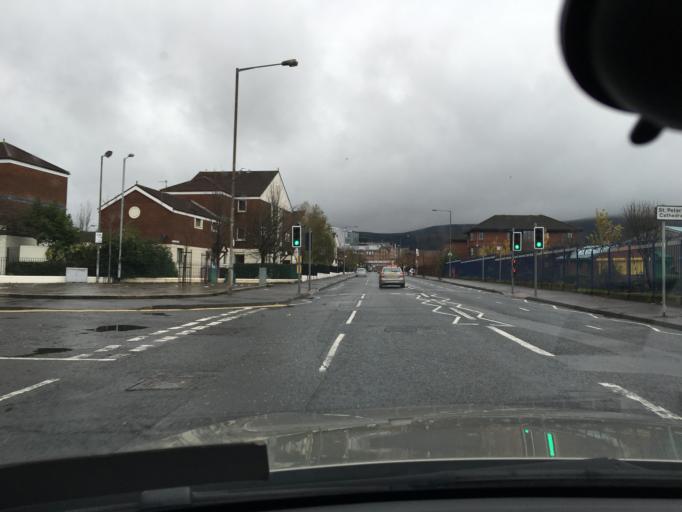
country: GB
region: Northern Ireland
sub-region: City of Belfast
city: Belfast
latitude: 54.5953
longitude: -5.9452
